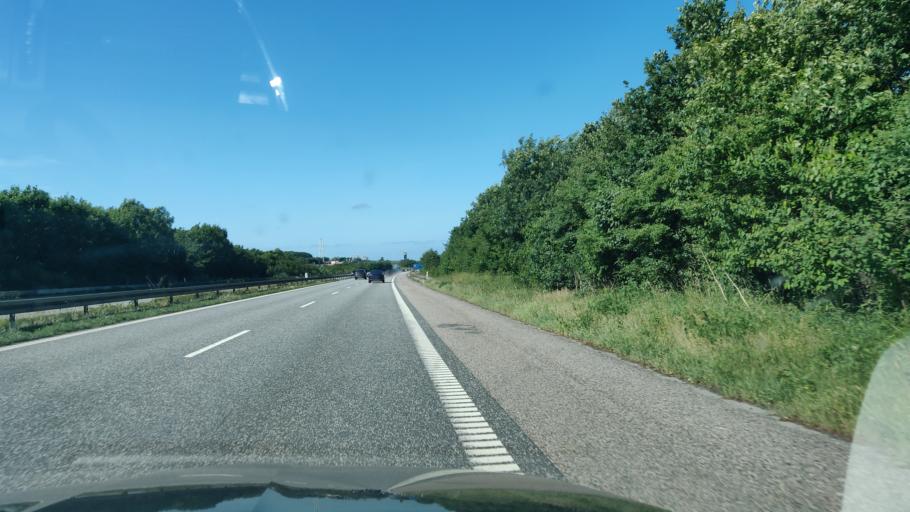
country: DK
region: North Denmark
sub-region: Mariagerfjord Kommune
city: Hobro
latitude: 56.7742
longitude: 9.6944
